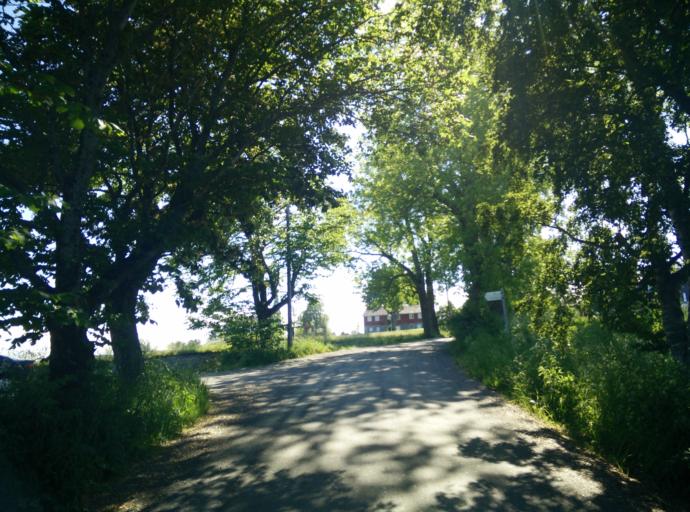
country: NO
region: Sor-Trondelag
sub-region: Trondheim
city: Trondheim
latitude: 63.4072
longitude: 10.3719
